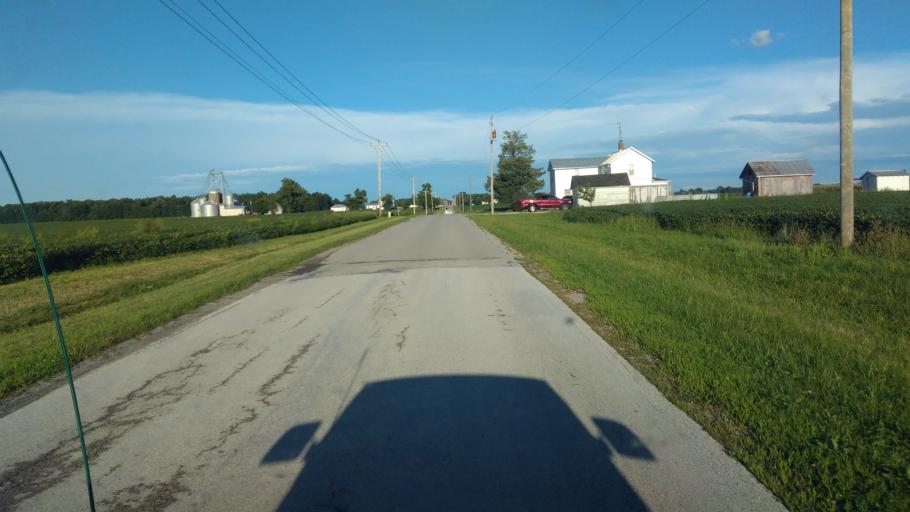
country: US
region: Ohio
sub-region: Wyandot County
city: Upper Sandusky
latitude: 40.8470
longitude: -83.3214
